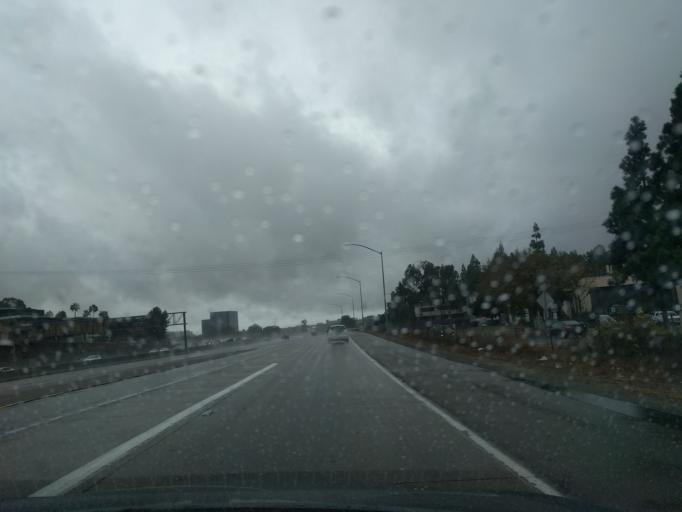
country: US
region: California
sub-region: San Diego County
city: San Diego
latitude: 32.7790
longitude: -117.1155
